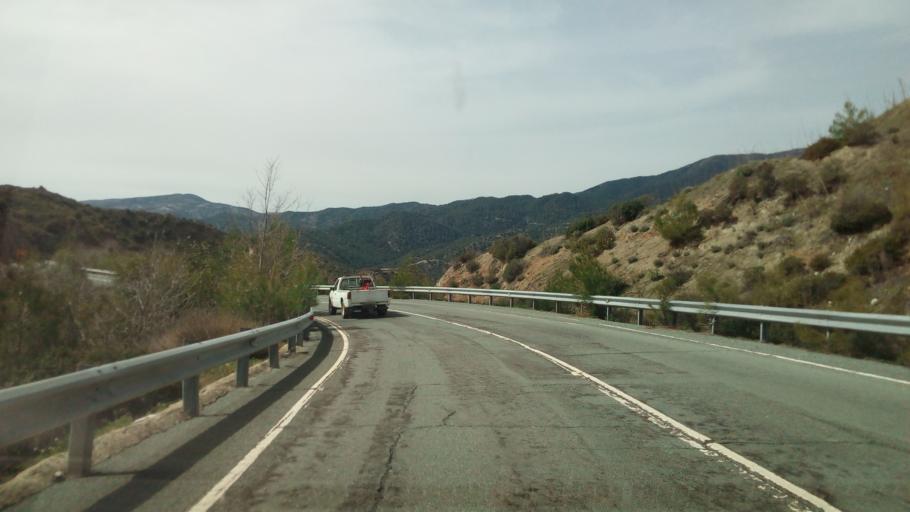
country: CY
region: Limassol
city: Pelendri
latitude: 34.8764
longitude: 32.9409
